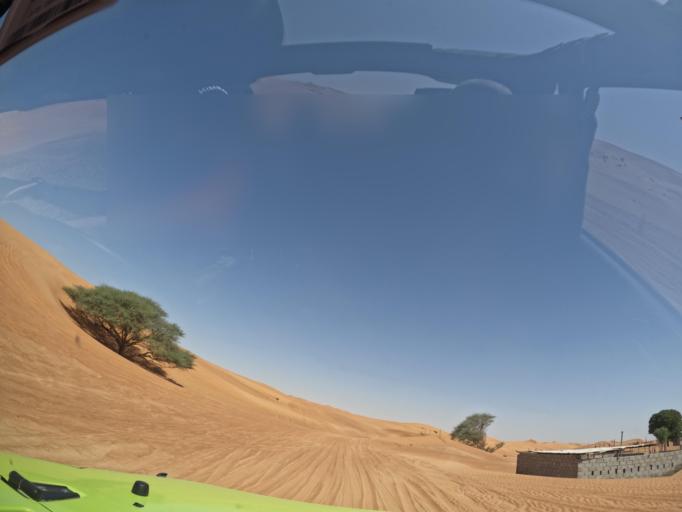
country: AE
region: Ash Shariqah
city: Adh Dhayd
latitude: 24.9902
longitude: 55.7239
